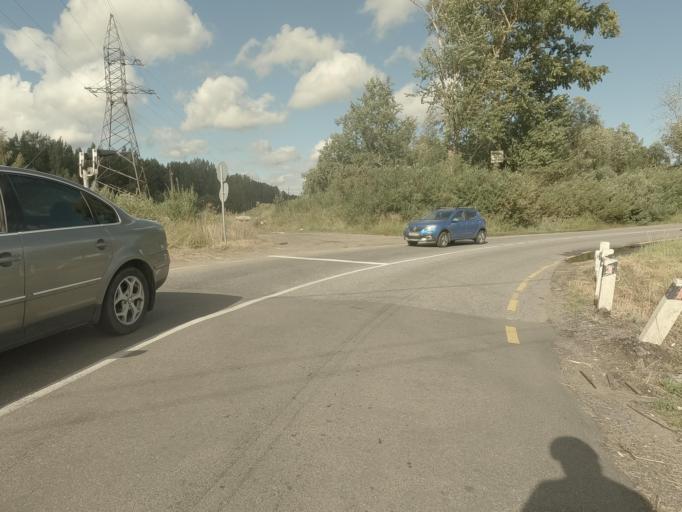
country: RU
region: Leningrad
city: Romanovka
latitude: 60.0245
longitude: 30.7000
